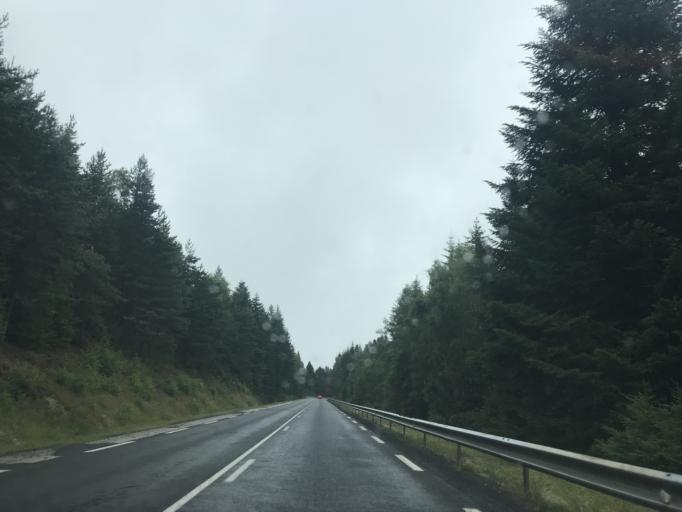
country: FR
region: Auvergne
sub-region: Departement de la Haute-Loire
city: Fontannes
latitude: 45.3399
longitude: 3.7108
